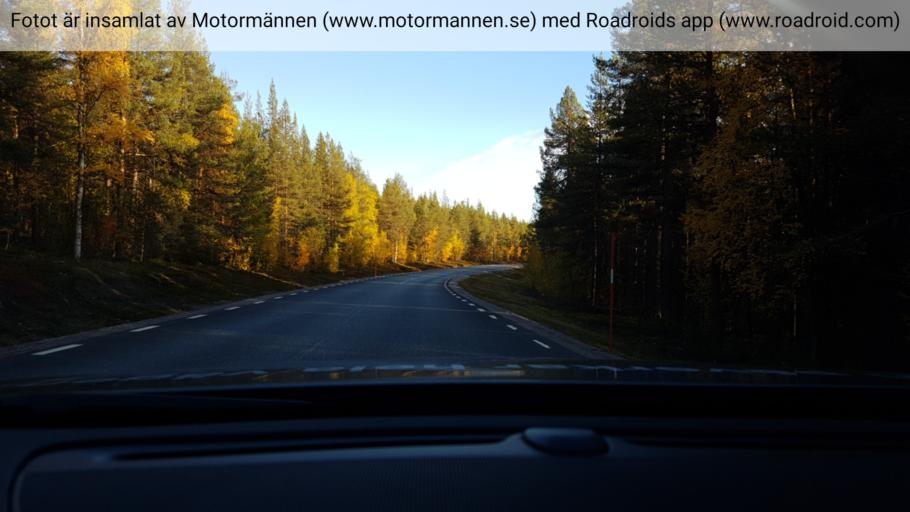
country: SE
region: Norrbotten
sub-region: Jokkmokks Kommun
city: Jokkmokk
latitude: 66.9385
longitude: 19.8116
